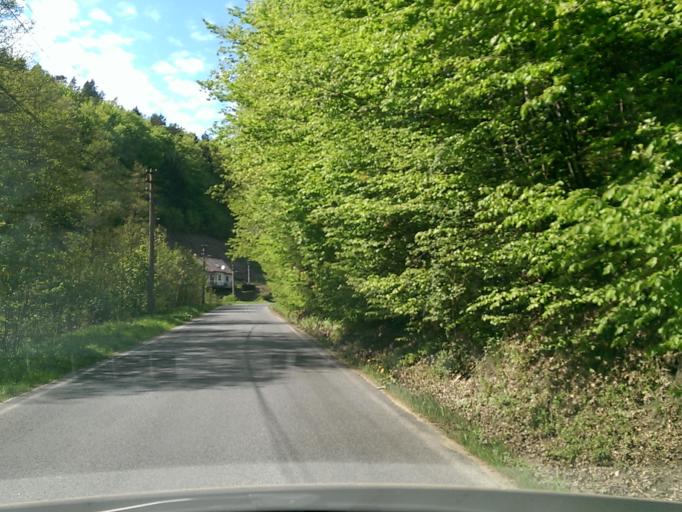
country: CZ
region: Liberecky
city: Mala Skala
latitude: 50.6573
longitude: 15.2170
